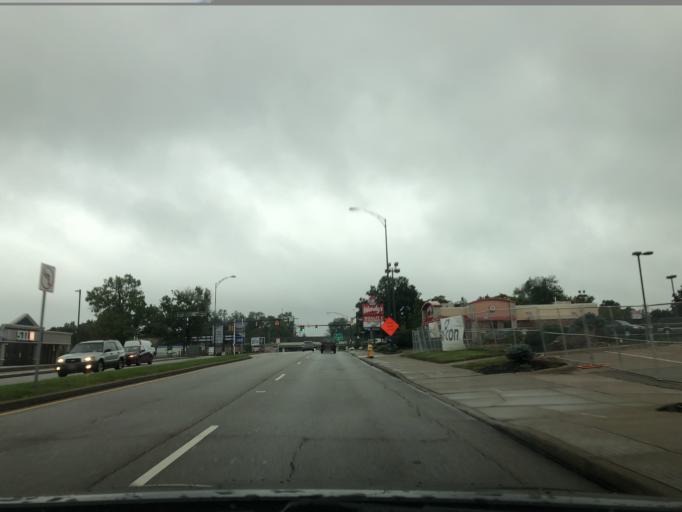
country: US
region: Ohio
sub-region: Hamilton County
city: Deer Park
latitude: 39.1973
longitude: -84.3806
